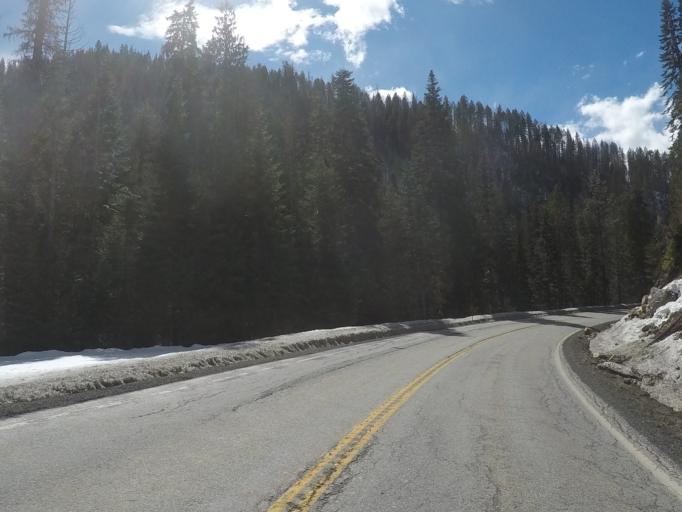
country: US
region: Montana
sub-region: Mineral County
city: Superior
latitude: 46.4771
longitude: -114.8742
